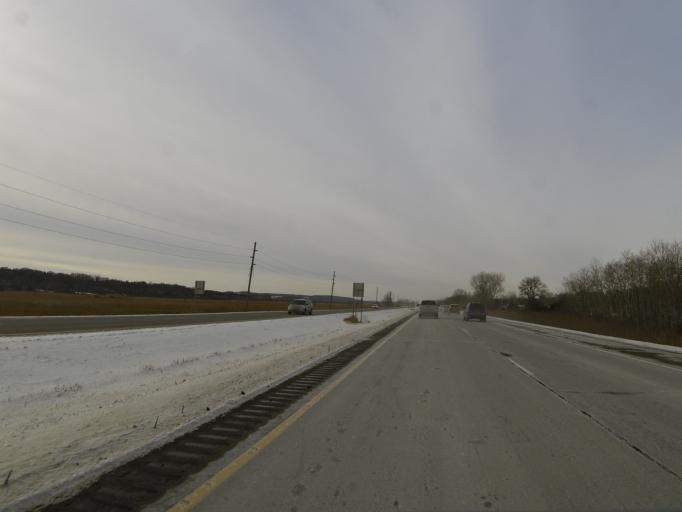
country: US
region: Minnesota
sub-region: Scott County
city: Jordan
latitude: 44.6688
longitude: -93.6447
